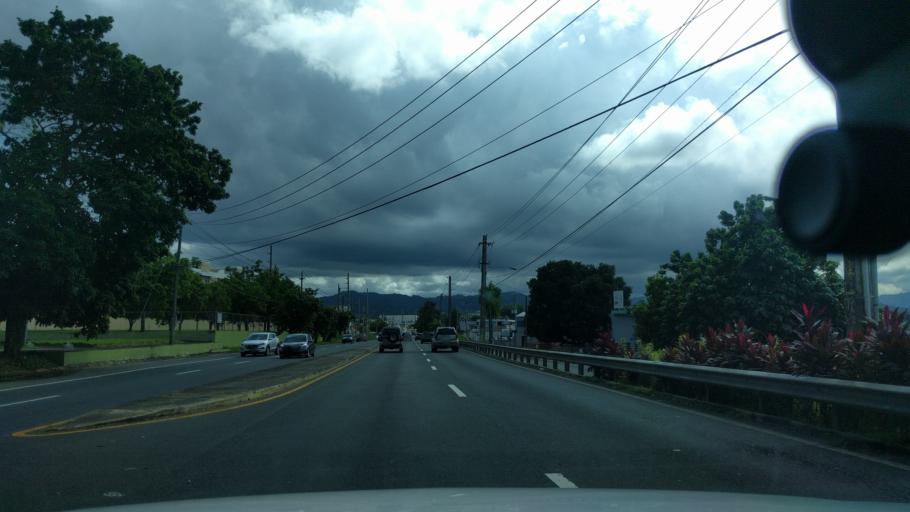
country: PR
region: Toa Alta
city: Pajaros
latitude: 18.3552
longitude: -66.1896
